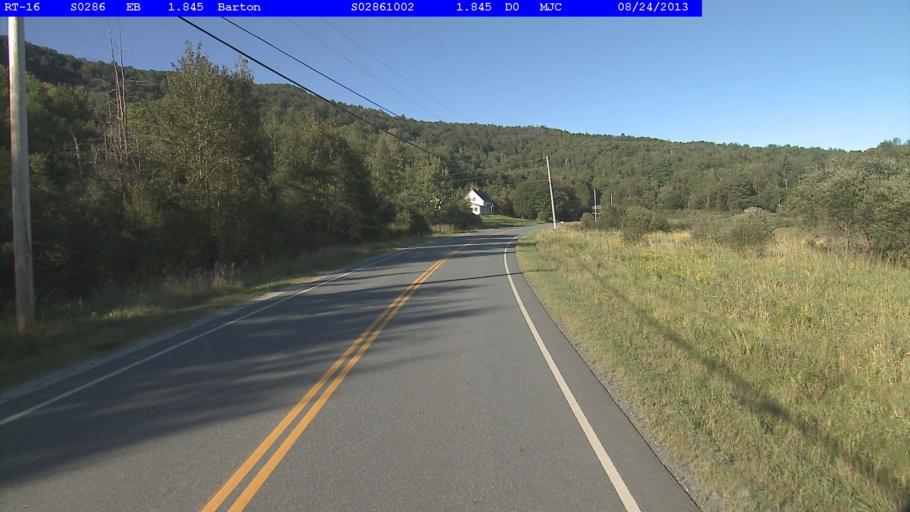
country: US
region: Vermont
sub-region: Orleans County
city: Newport
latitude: 44.7618
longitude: -72.1481
